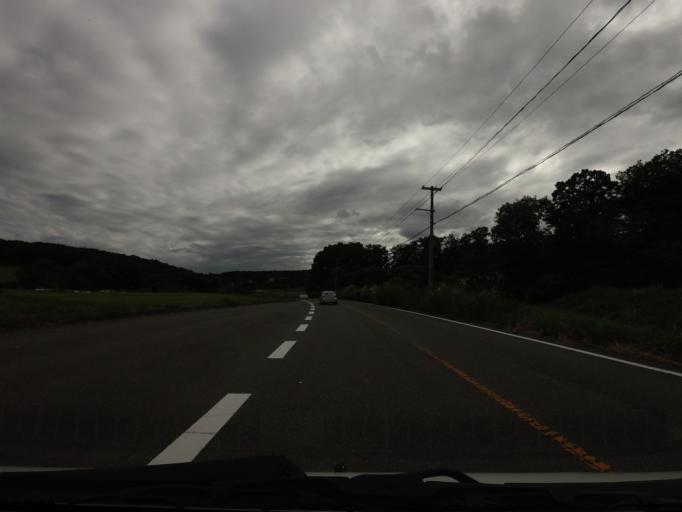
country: JP
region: Fukushima
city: Nihommatsu
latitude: 37.5885
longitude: 140.3536
